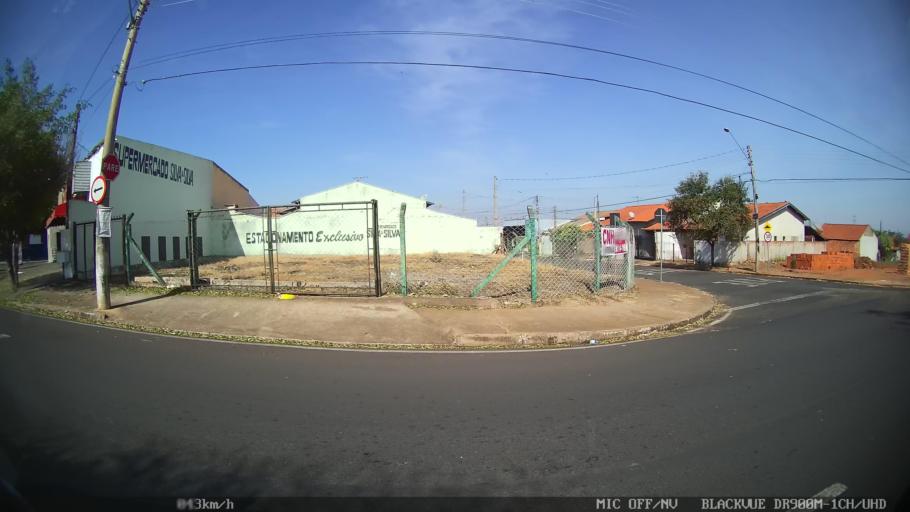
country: BR
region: Sao Paulo
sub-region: Sao Jose Do Rio Preto
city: Sao Jose do Rio Preto
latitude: -20.7910
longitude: -49.4388
